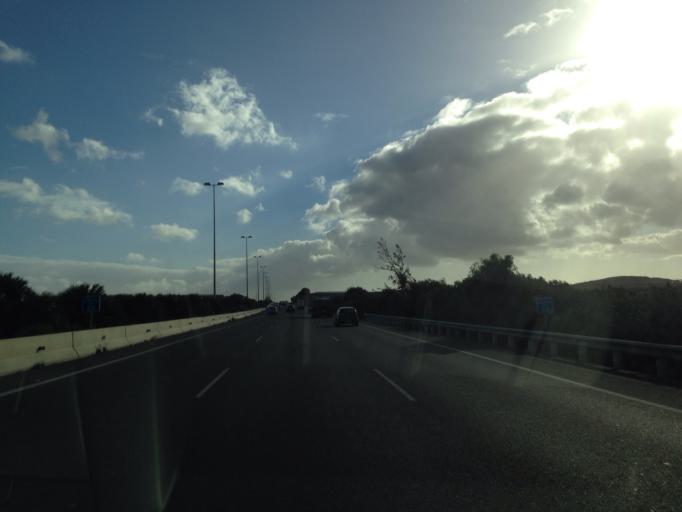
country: ES
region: Canary Islands
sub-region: Provincia de Las Palmas
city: Cruce de Arinaga
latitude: 27.8921
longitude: -15.4077
